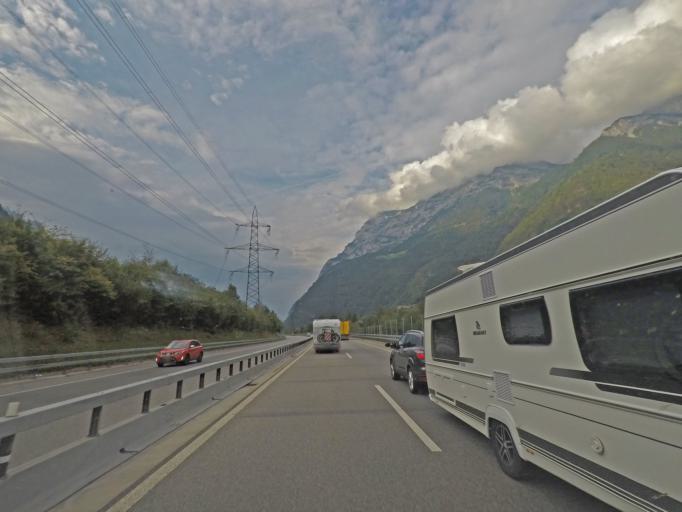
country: CH
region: Uri
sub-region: Uri
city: Silenen
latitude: 46.7973
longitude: 8.6644
